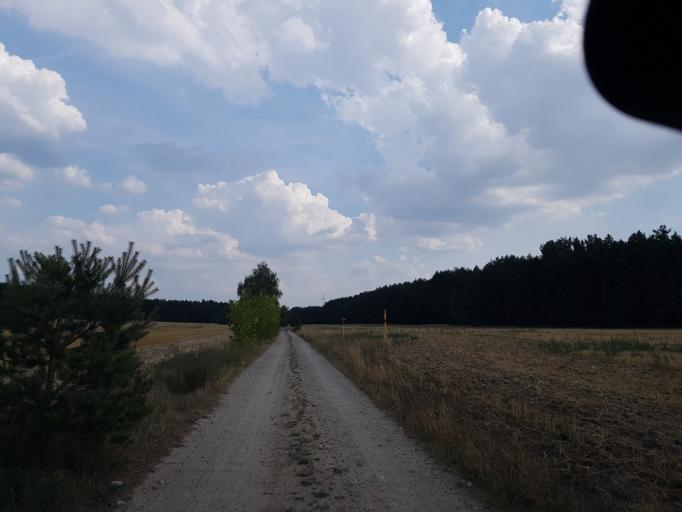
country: DE
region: Brandenburg
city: Treuenbrietzen
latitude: 52.0372
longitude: 12.8704
